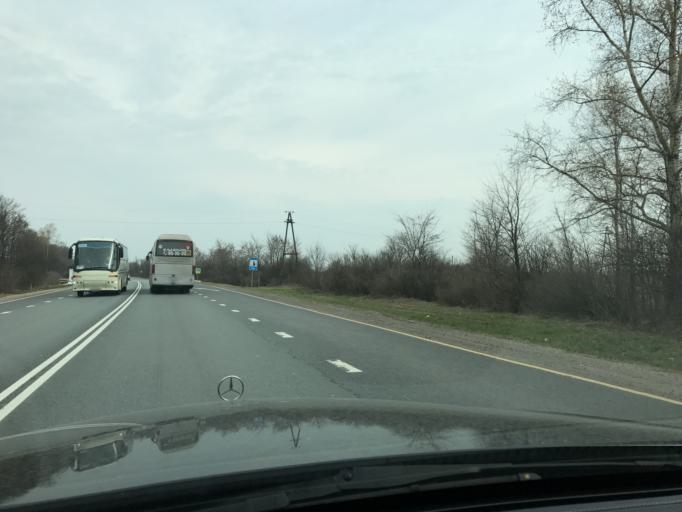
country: RU
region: Vladimir
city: Suzdal'
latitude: 56.3742
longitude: 40.4611
